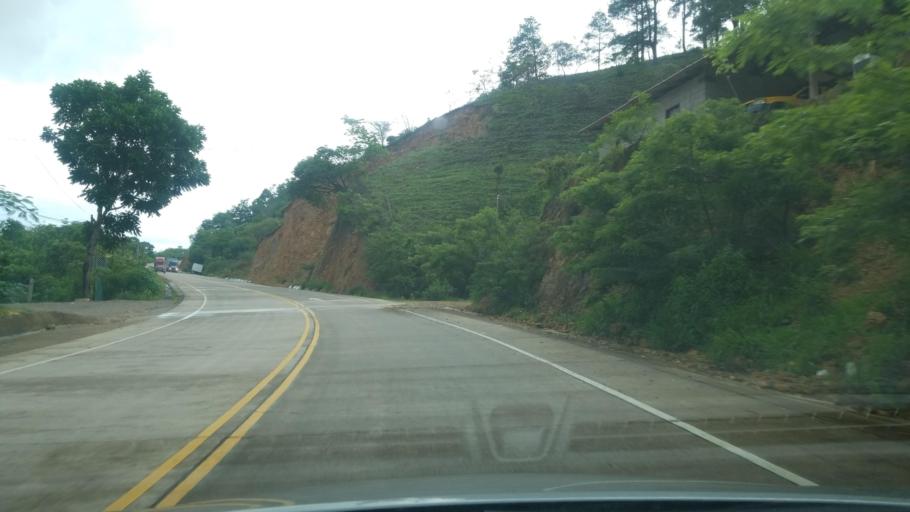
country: HN
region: Copan
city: Copan
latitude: 14.8397
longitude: -89.1799
